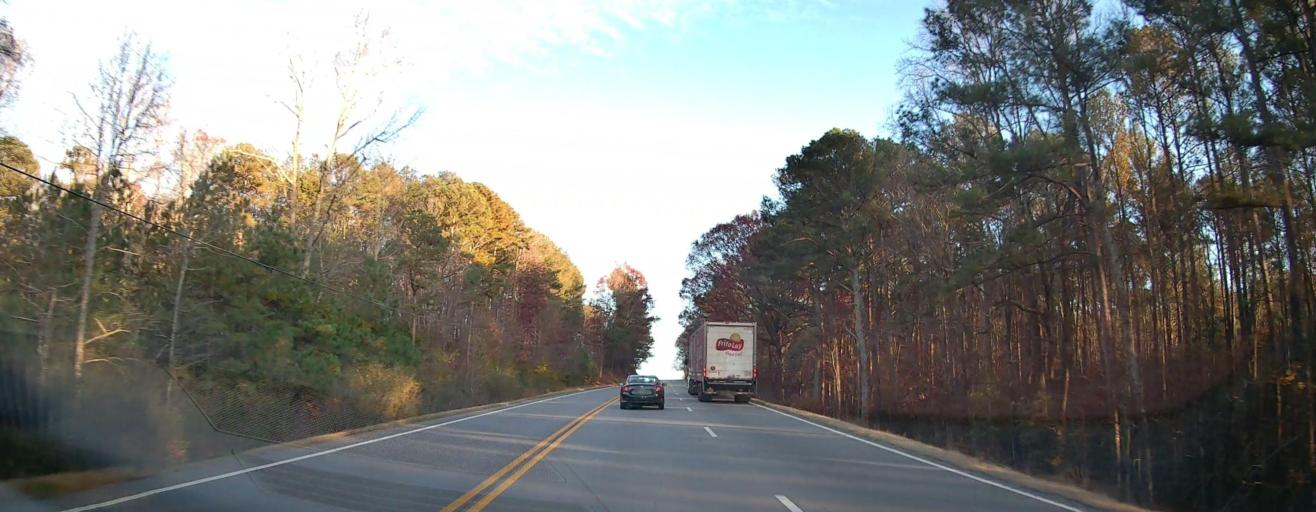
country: US
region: Alabama
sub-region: Saint Clair County
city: Steele
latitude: 34.0668
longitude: -86.2504
